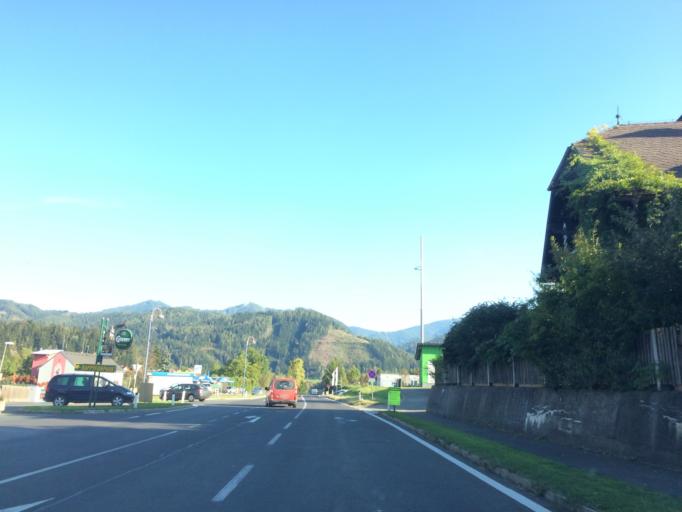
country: AT
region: Styria
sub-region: Politischer Bezirk Leoben
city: Sankt Michael in Obersteiermark
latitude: 47.3378
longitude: 15.0155
